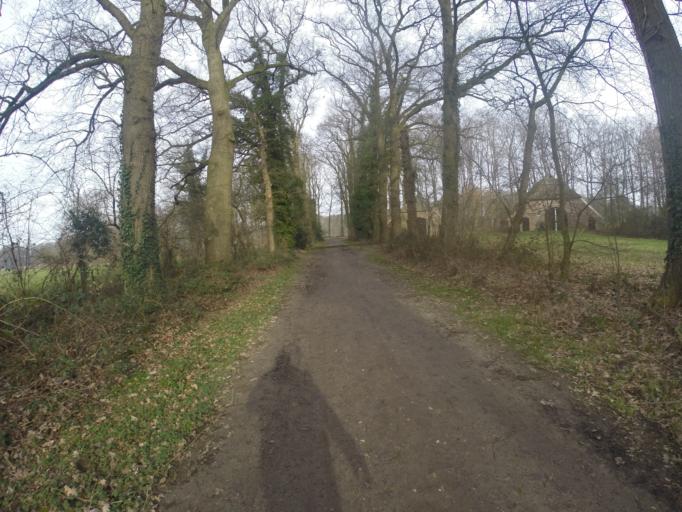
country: NL
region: Gelderland
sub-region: Gemeente Bronckhorst
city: Hengelo
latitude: 52.0976
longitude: 6.2860
